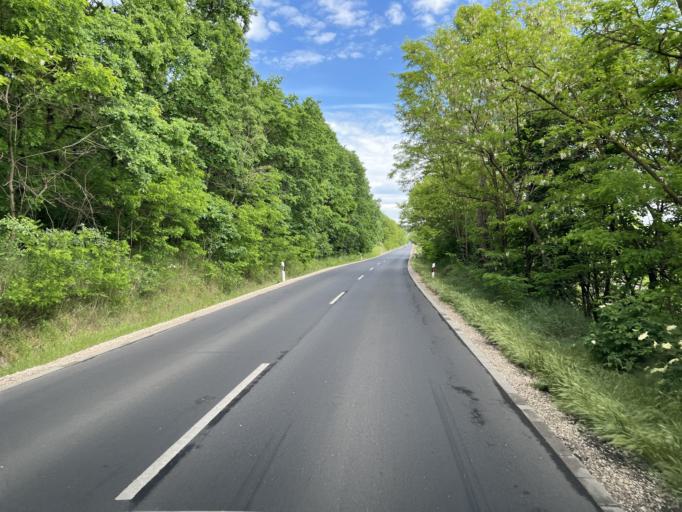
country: HU
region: Pest
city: Pecel
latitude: 47.5113
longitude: 19.3698
